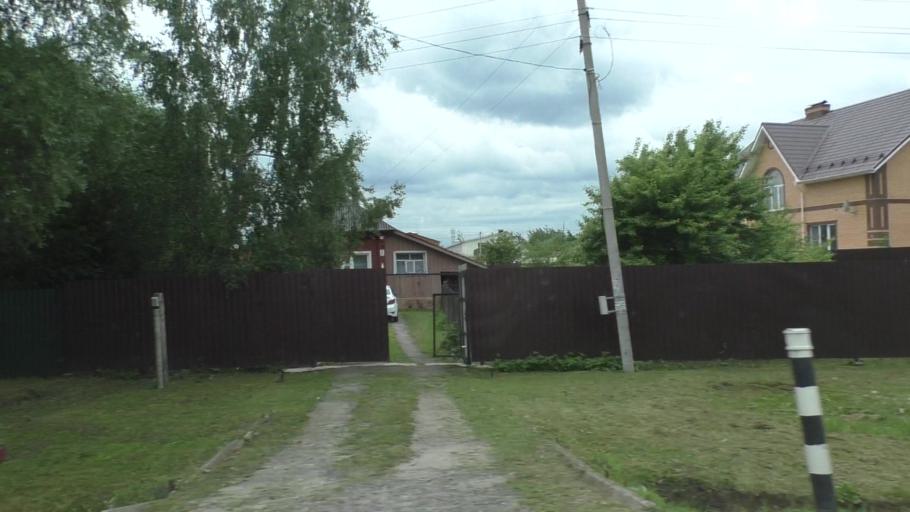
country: RU
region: Moskovskaya
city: Yegor'yevsk
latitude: 55.3987
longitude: 39.0120
